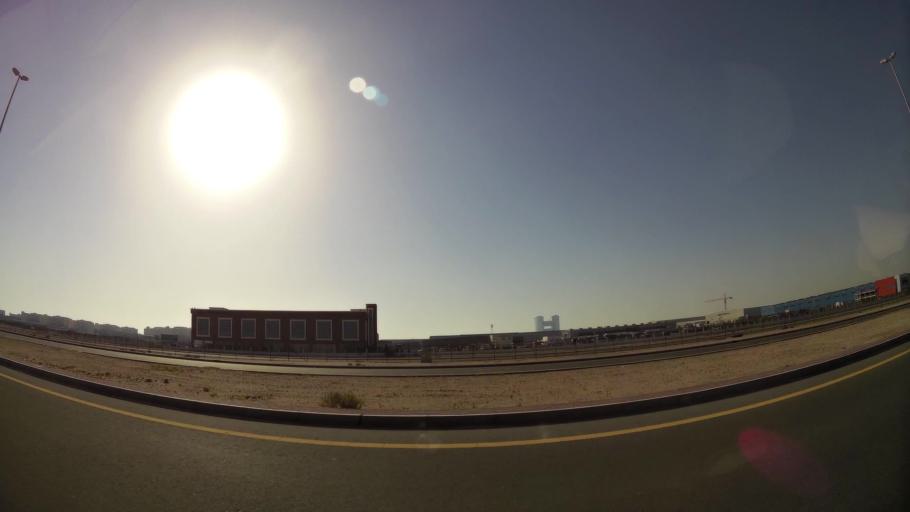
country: AE
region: Dubai
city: Dubai
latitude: 24.9493
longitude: 55.0923
